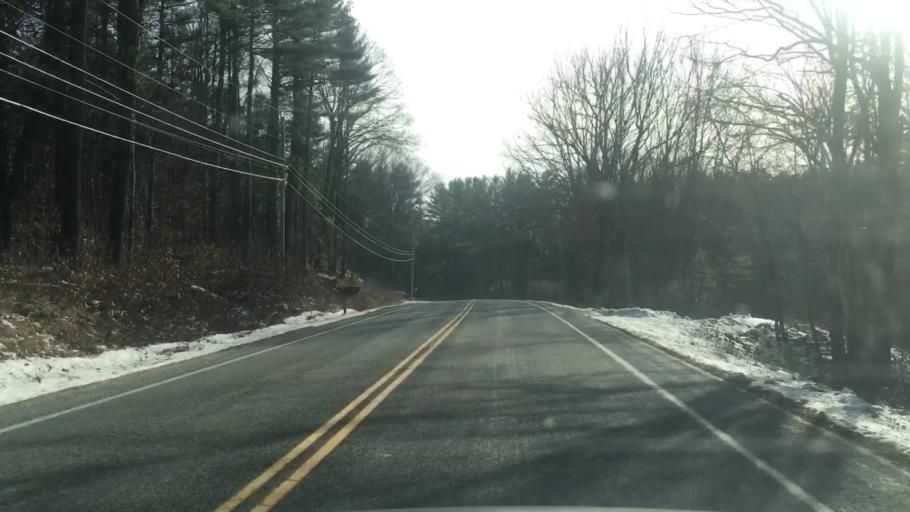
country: US
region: New Hampshire
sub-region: Merrimack County
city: Canterbury
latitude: 43.2981
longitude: -71.5636
